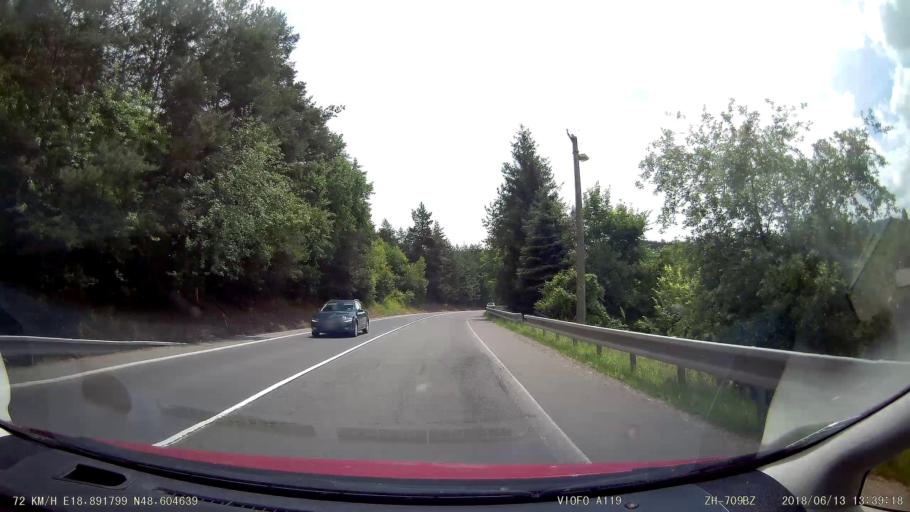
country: SK
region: Banskobystricky
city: Ziar nad Hronom
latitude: 48.6045
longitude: 18.8918
